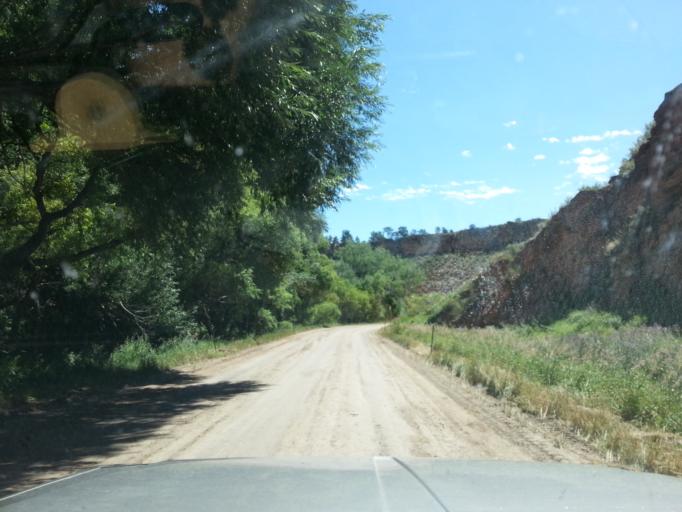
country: US
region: Colorado
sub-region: Larimer County
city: Laporte
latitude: 40.4807
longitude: -105.2224
